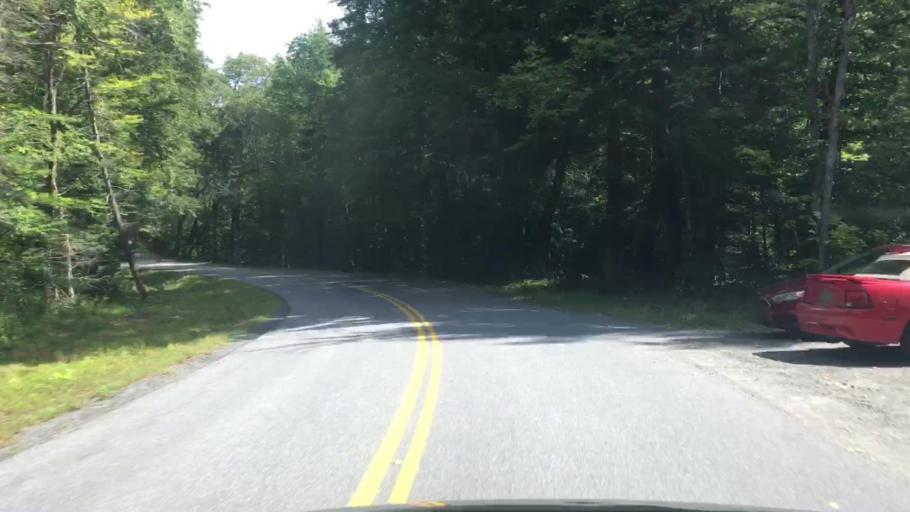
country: US
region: Vermont
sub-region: Windham County
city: West Brattleboro
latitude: 42.8130
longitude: -72.7299
